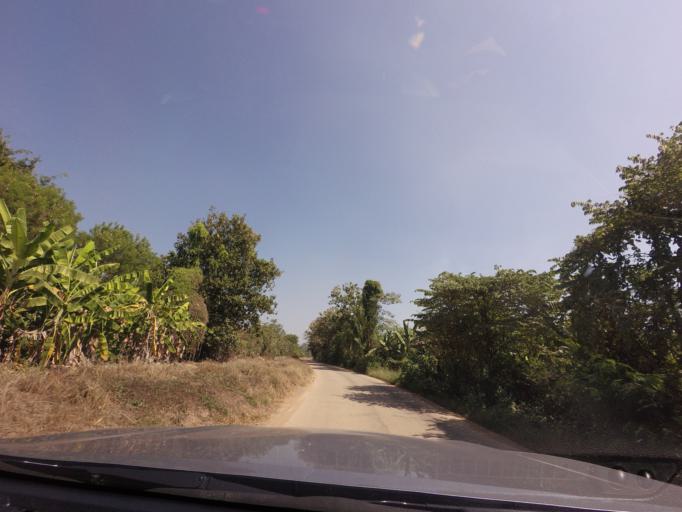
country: TH
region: Sukhothai
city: Sawankhalok
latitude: 17.2761
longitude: 99.8236
